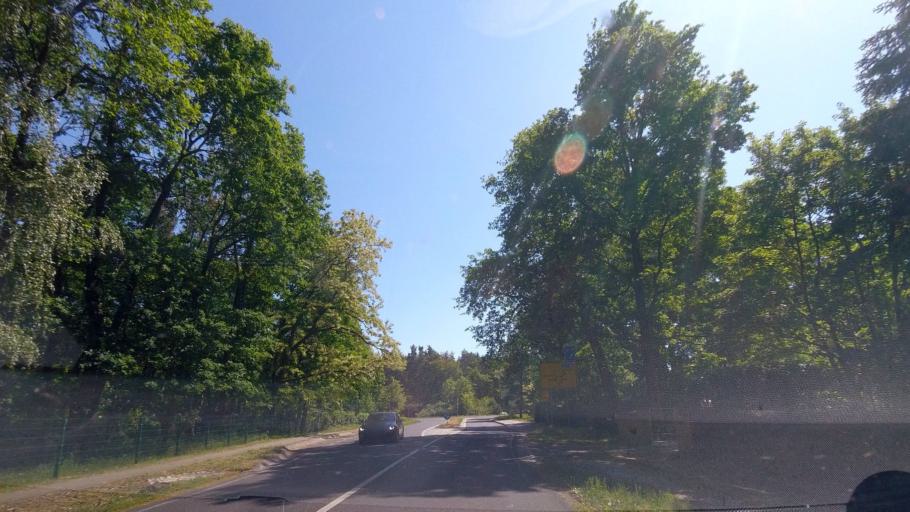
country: DE
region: Brandenburg
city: Gross Kreutz
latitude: 52.3488
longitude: 12.7651
